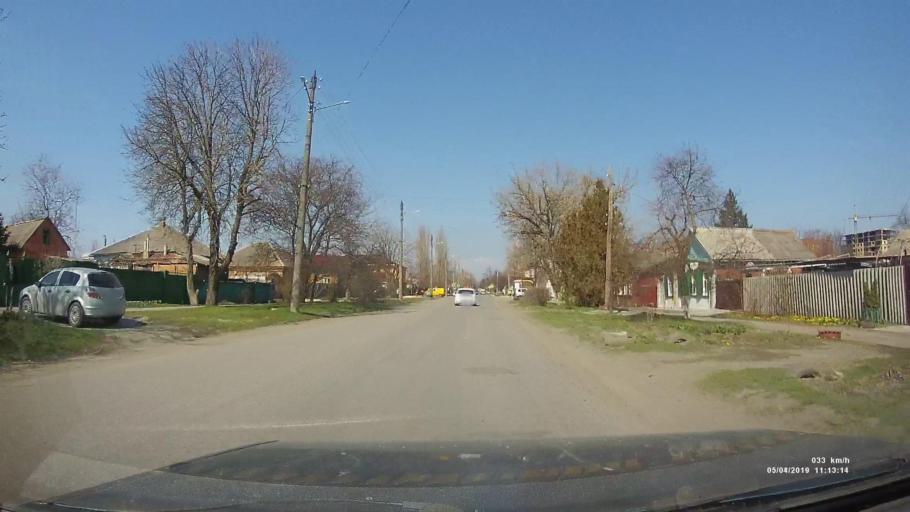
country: RU
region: Rostov
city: Azov
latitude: 47.1014
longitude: 39.4325
